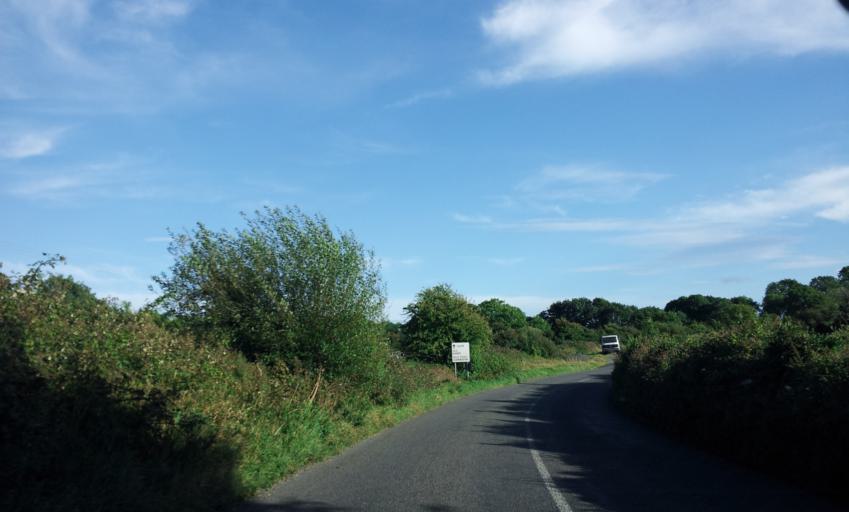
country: IE
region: Munster
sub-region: An Clar
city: Ennis
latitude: 52.9550
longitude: -9.0716
